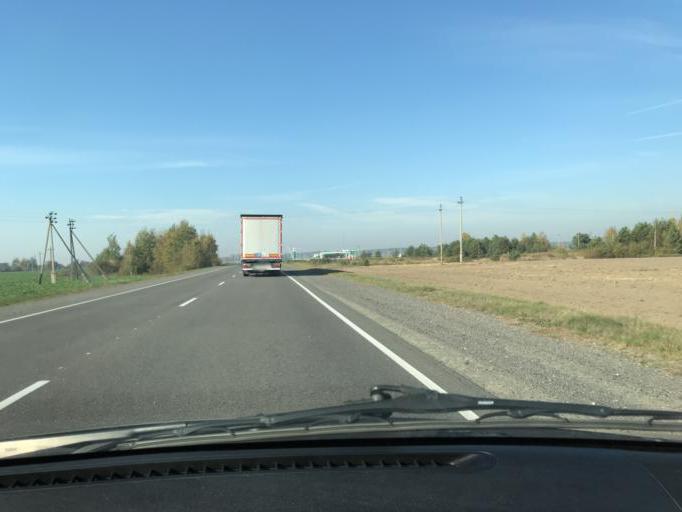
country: BY
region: Brest
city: Horad Luninyets
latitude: 52.3162
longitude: 26.6369
